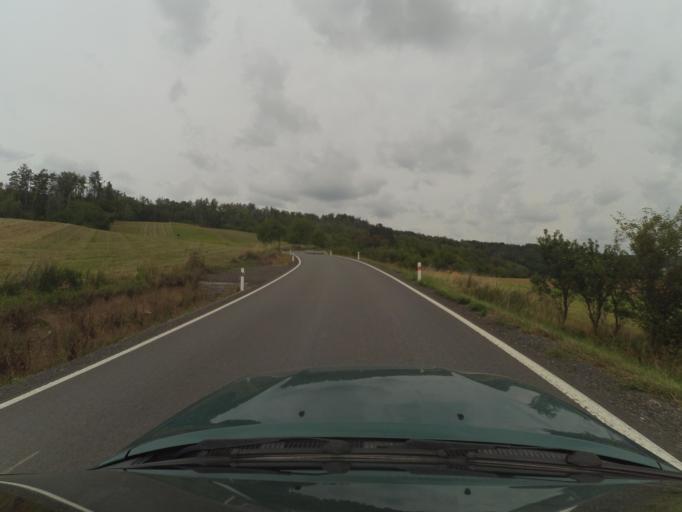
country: CZ
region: Central Bohemia
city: Revnicov
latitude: 50.1978
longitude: 13.7483
